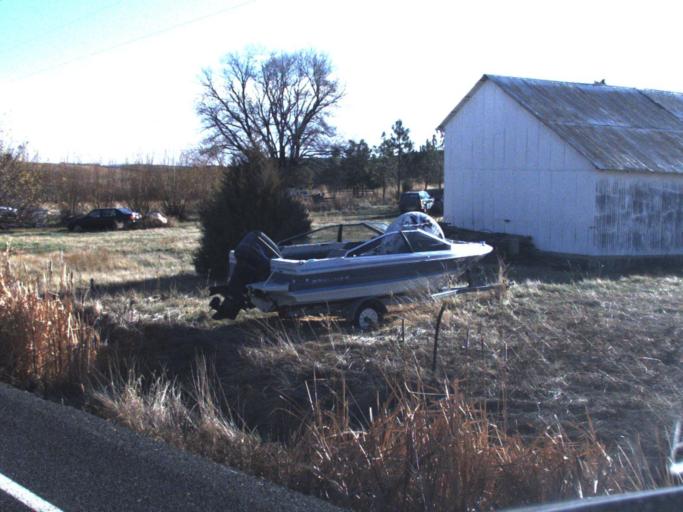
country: US
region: Washington
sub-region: Whitman County
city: Colfax
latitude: 46.7375
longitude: -117.3511
